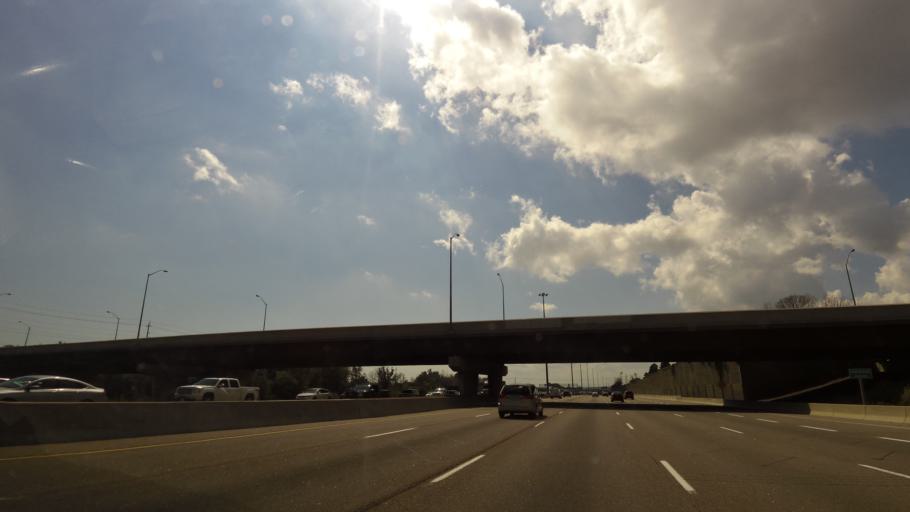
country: CA
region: Ontario
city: Ajax
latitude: 43.8534
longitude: -79.0215
